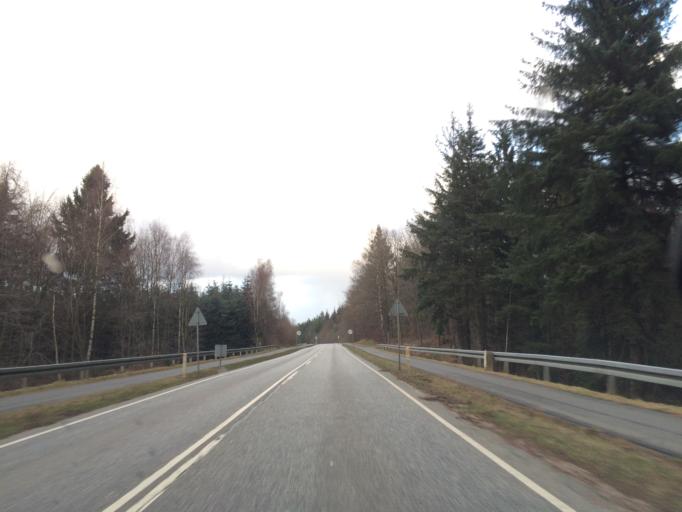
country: DK
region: Central Jutland
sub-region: Silkeborg Kommune
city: Virklund
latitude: 56.1172
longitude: 9.5659
